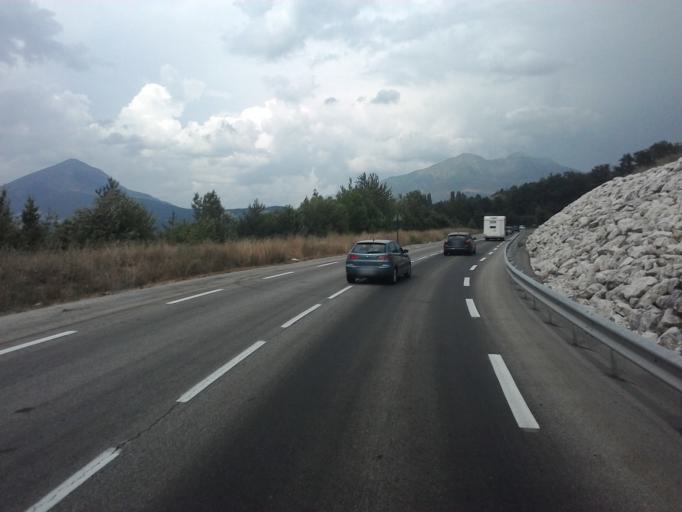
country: FR
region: Rhone-Alpes
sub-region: Departement de l'Isere
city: La Mure
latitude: 44.8921
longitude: 5.8153
